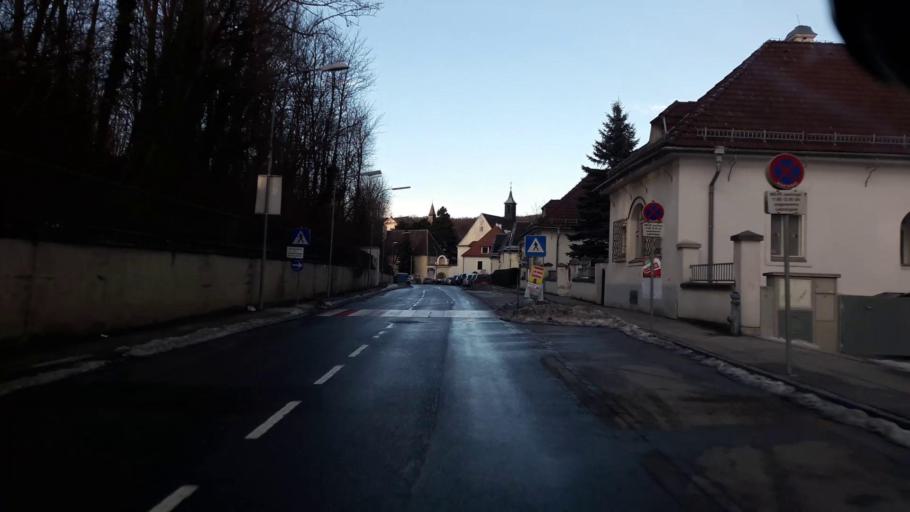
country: AT
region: Lower Austria
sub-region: Politischer Bezirk Wien-Umgebung
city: Mauerbach
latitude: 48.2479
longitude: 16.1663
